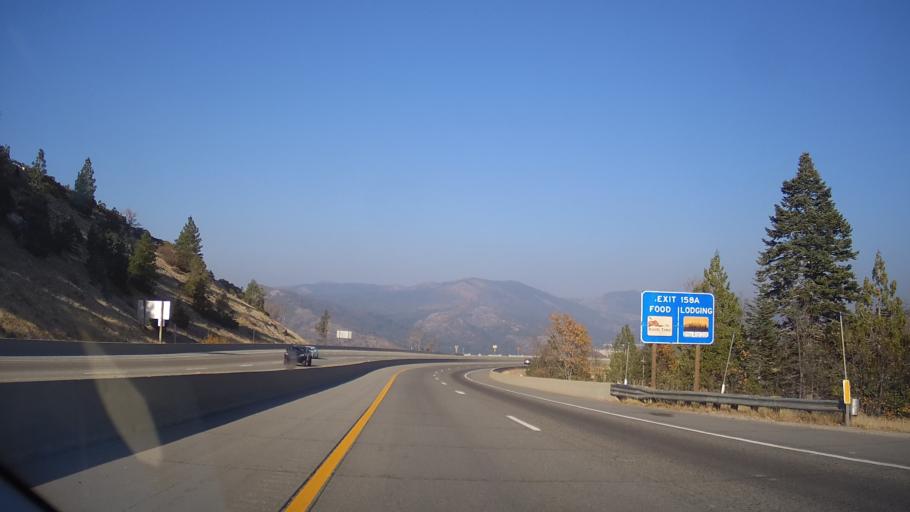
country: US
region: California
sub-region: Sierra County
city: Downieville
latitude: 39.2977
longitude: -120.6738
